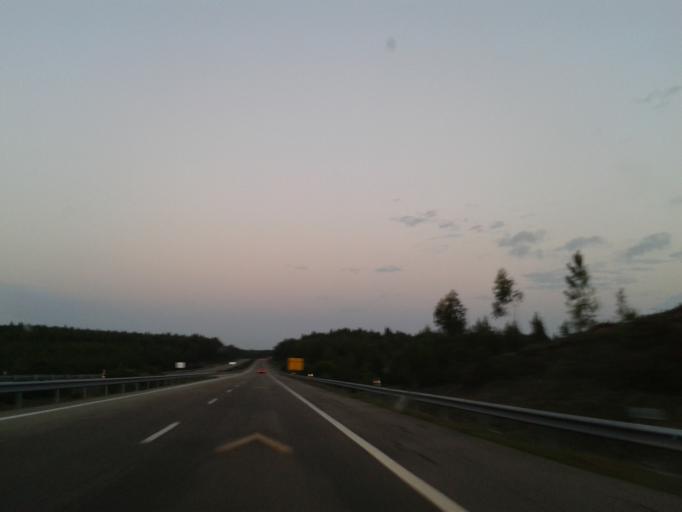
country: PT
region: Evora
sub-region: Vendas Novas
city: Vendas Novas
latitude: 38.6270
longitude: -8.5570
